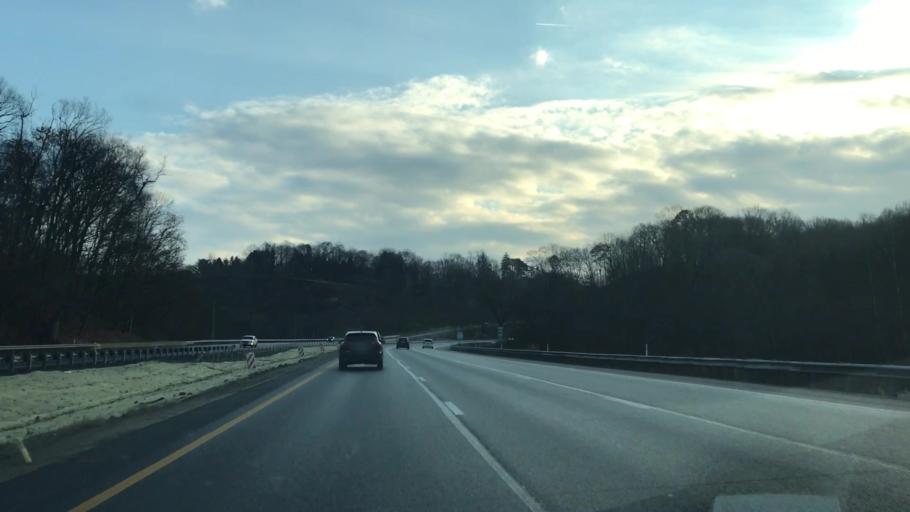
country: US
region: Pennsylvania
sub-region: Allegheny County
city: Avalon
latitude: 40.5198
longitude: -80.0600
